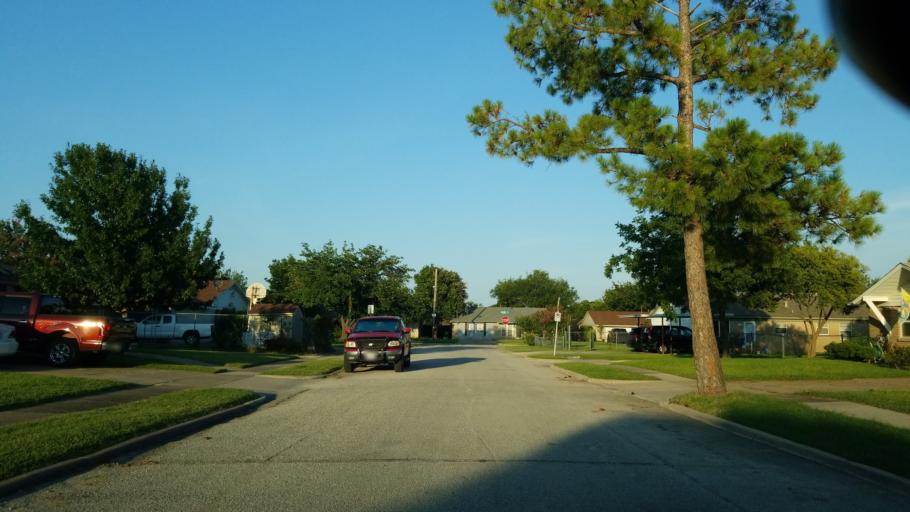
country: US
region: Texas
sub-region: Dallas County
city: Carrollton
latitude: 32.9477
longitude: -96.8889
